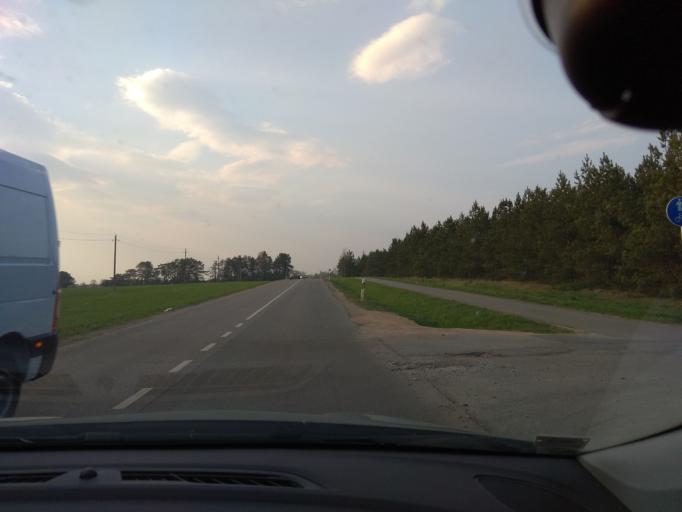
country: LT
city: Grigiskes
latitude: 54.6177
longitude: 25.1163
